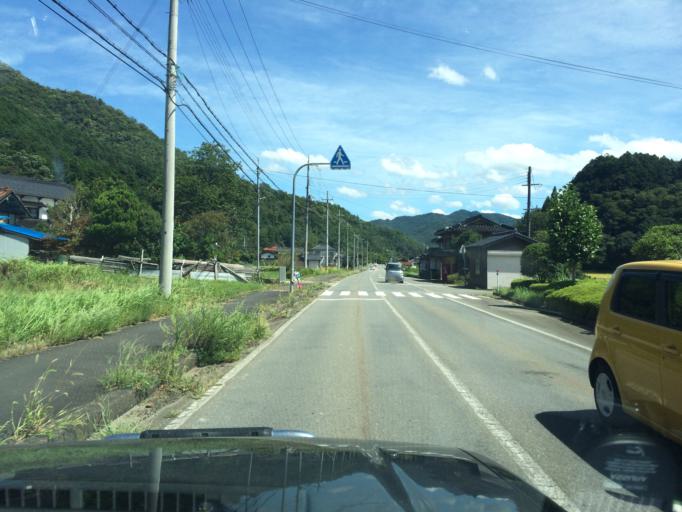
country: JP
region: Hyogo
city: Toyooka
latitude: 35.4650
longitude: 134.8370
